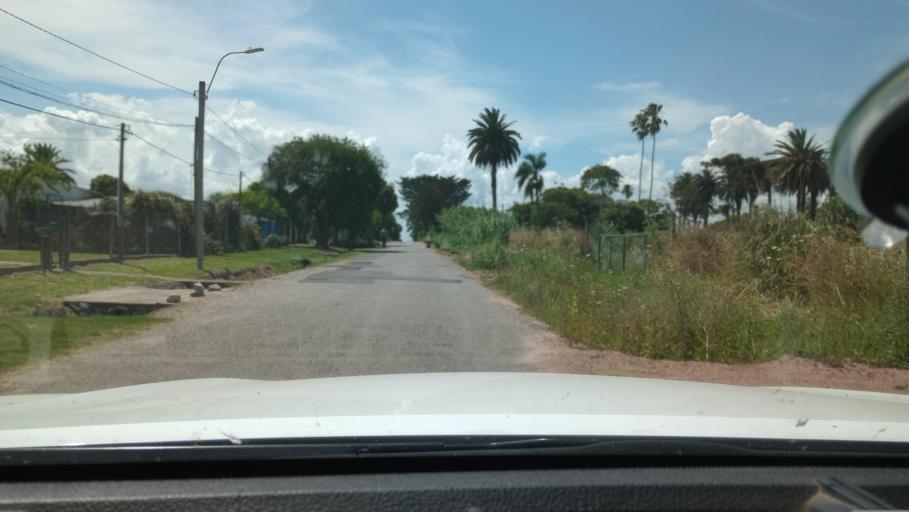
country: UY
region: Canelones
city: Joaquin Suarez
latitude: -34.7573
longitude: -56.0097
